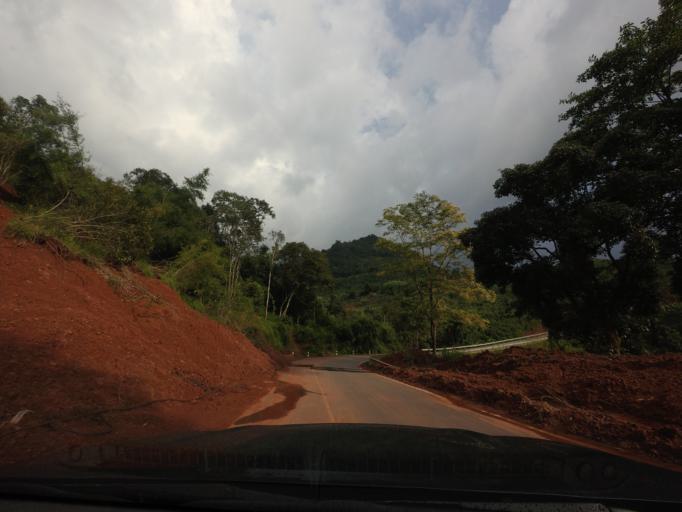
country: TH
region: Nan
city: Bo Kluea
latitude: 19.2631
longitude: 101.1788
